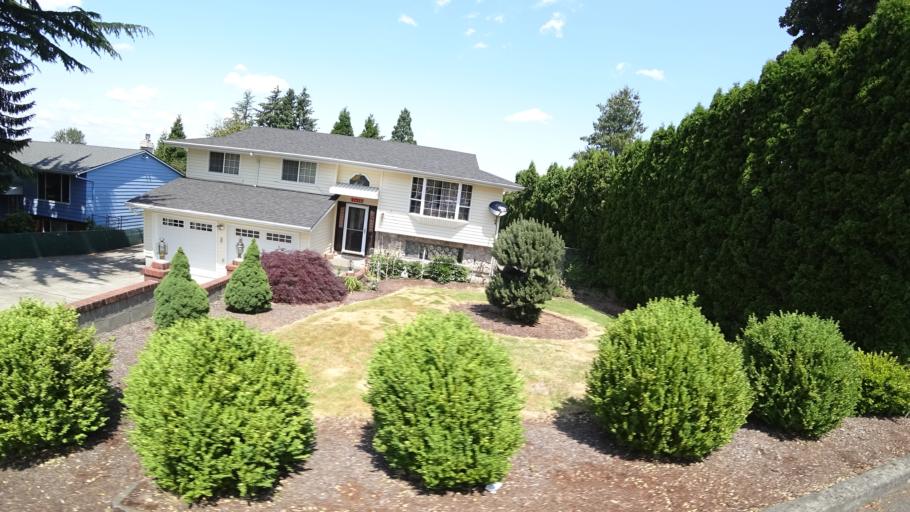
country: US
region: Oregon
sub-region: Multnomah County
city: Lents
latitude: 45.4613
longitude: -122.5660
